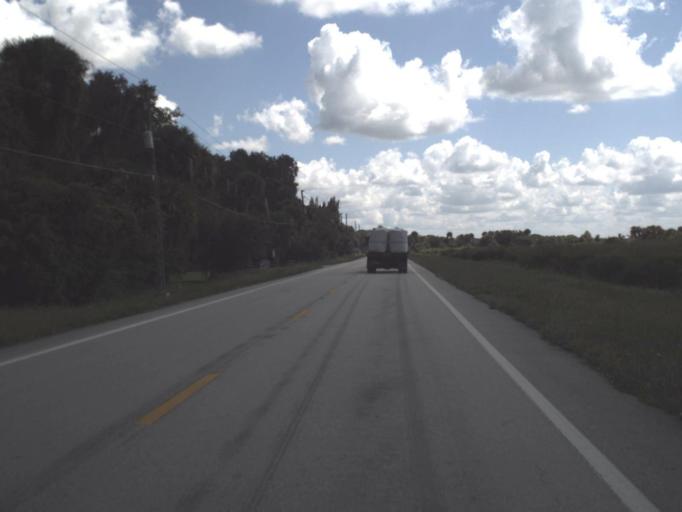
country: US
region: Florida
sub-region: Okeechobee County
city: Taylor Creek
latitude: 27.1553
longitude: -80.7044
